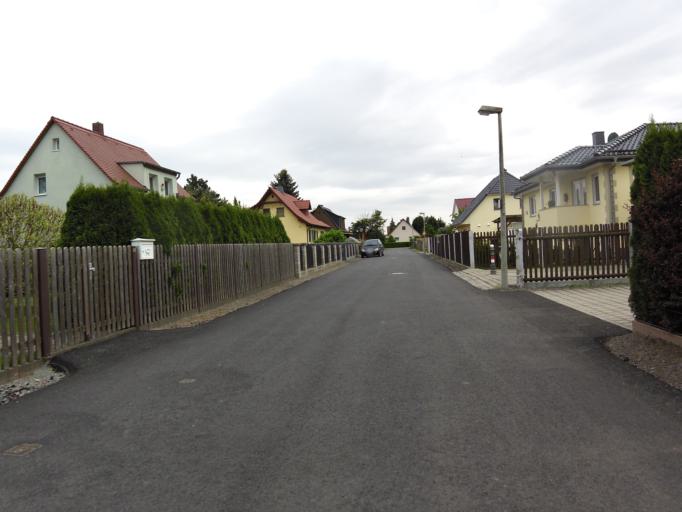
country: DE
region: Saxony
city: Zwenkau
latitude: 51.2788
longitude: 12.2968
